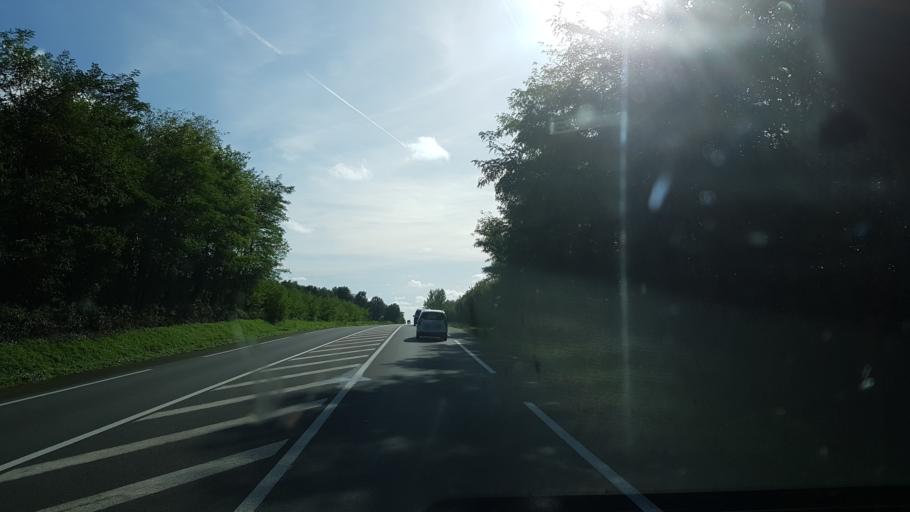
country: FR
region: Poitou-Charentes
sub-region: Departement de la Charente
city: Saint-Claud
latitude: 45.8559
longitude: 0.4641
